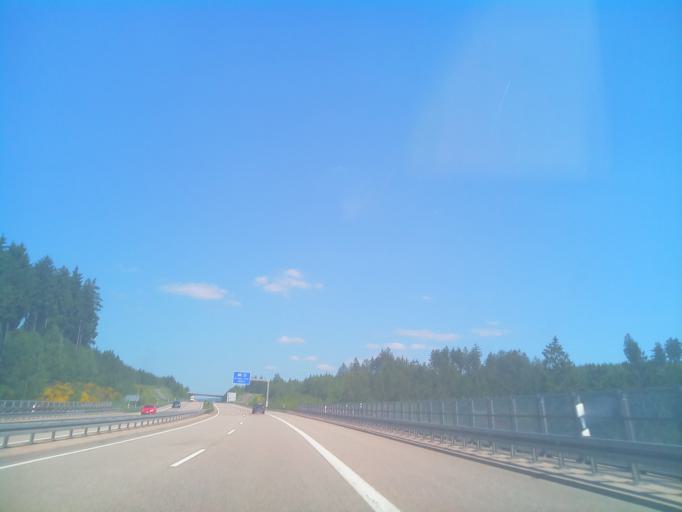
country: DE
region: Thuringia
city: Benshausen
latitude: 50.6133
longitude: 10.6092
